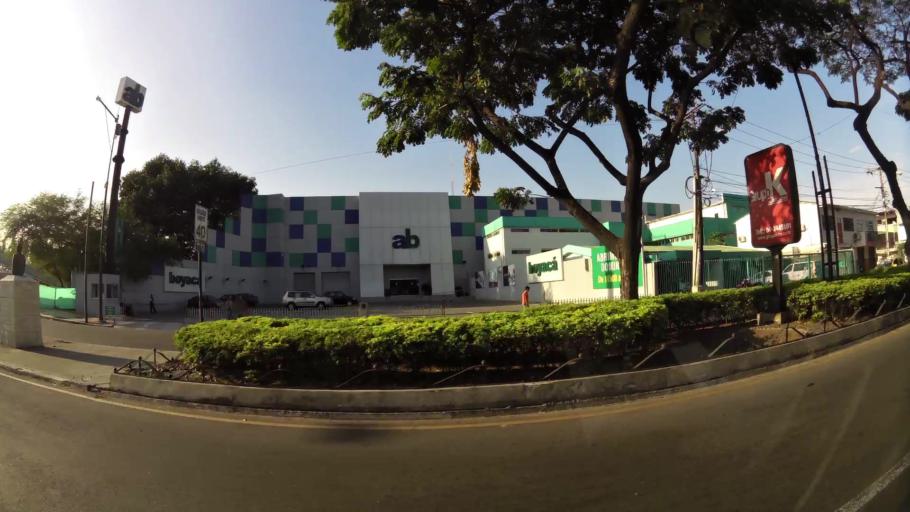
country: EC
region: Guayas
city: Guayaquil
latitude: -2.1776
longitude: -79.9030
